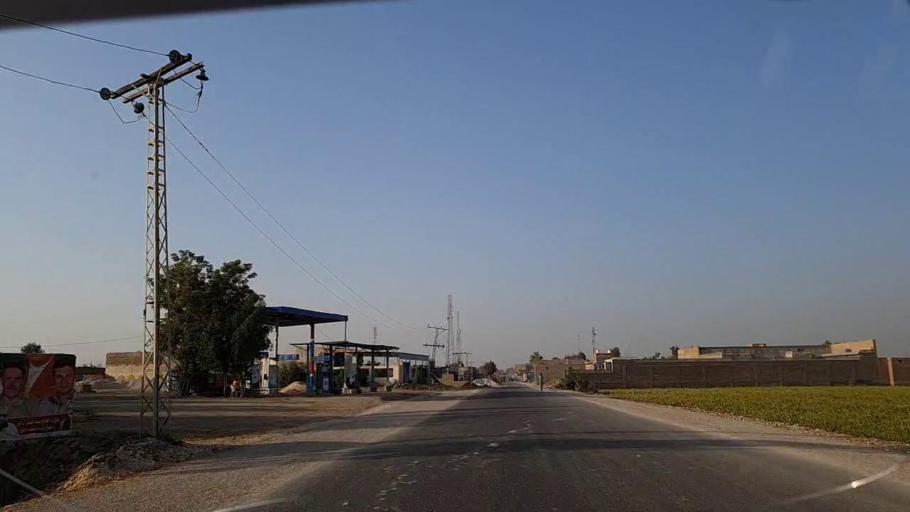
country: PK
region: Sindh
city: Rustam jo Goth
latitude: 27.9602
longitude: 68.8066
